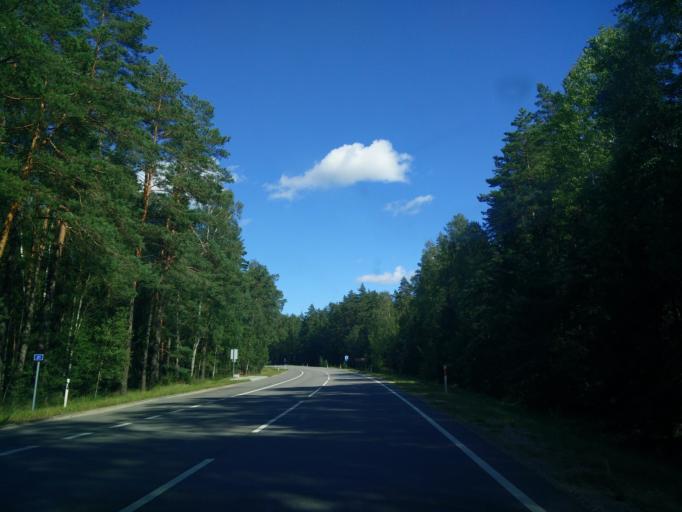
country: LT
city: Vilkija
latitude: 54.9621
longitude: 23.3722
